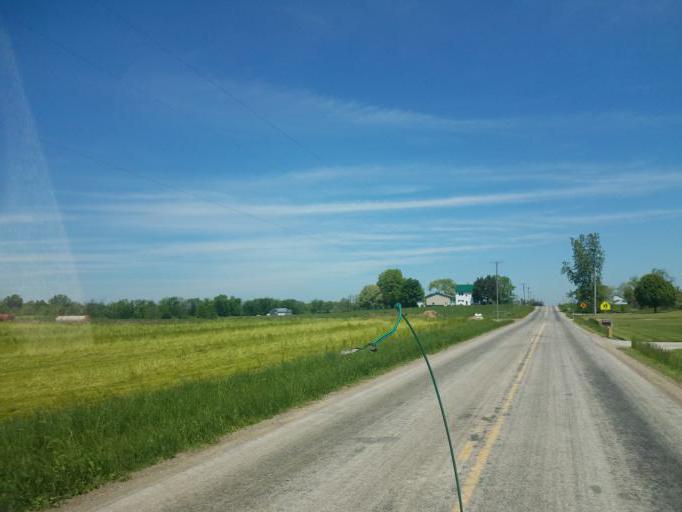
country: US
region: Ohio
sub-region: Ashland County
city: Ashland
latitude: 40.9280
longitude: -82.2433
